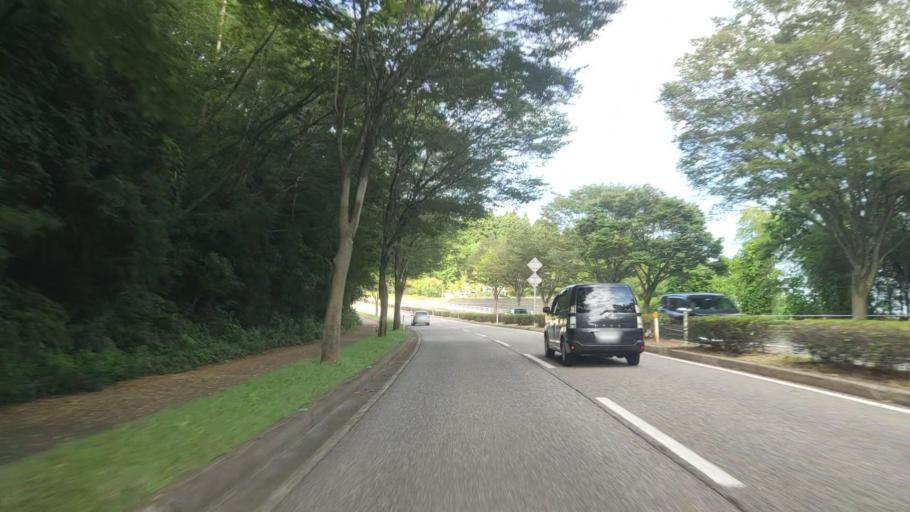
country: JP
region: Ishikawa
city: Matsuto
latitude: 36.4500
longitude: 136.5643
